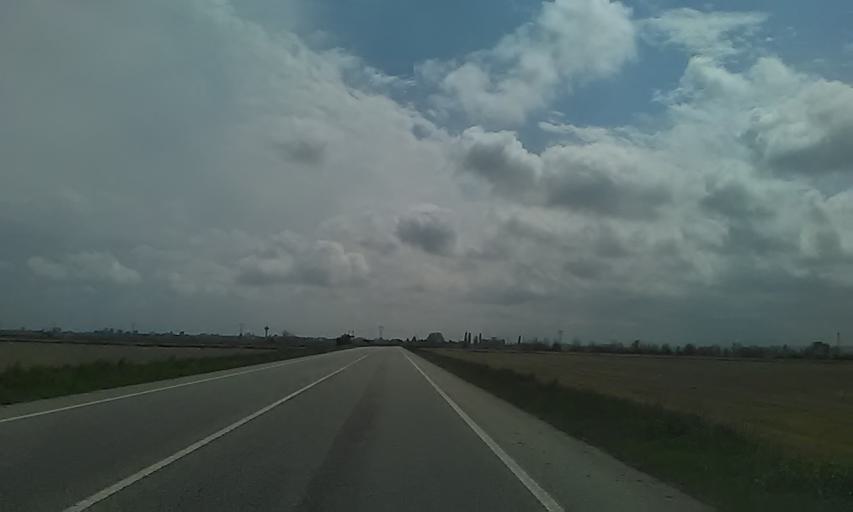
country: IT
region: Piedmont
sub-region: Provincia di Vercelli
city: Stroppiana
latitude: 45.2052
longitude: 8.4613
